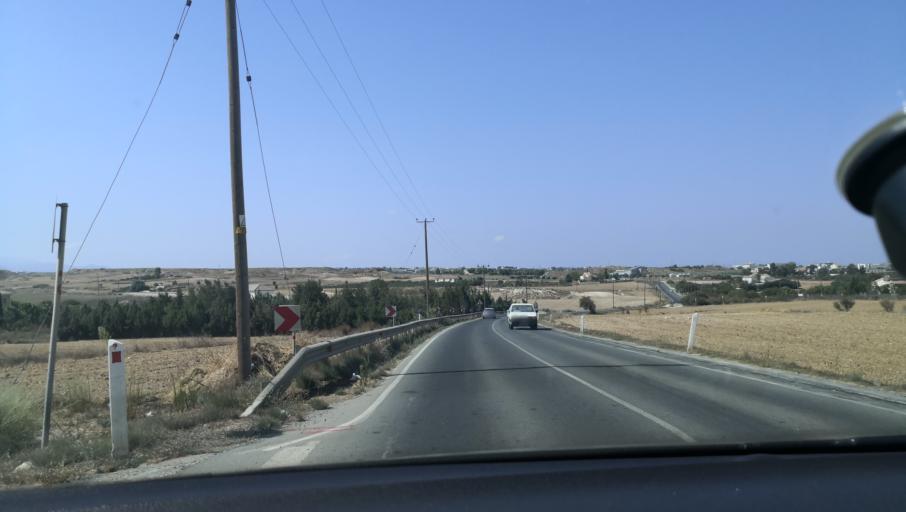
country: CY
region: Lefkosia
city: Kato Deftera
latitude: 35.1192
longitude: 33.2697
